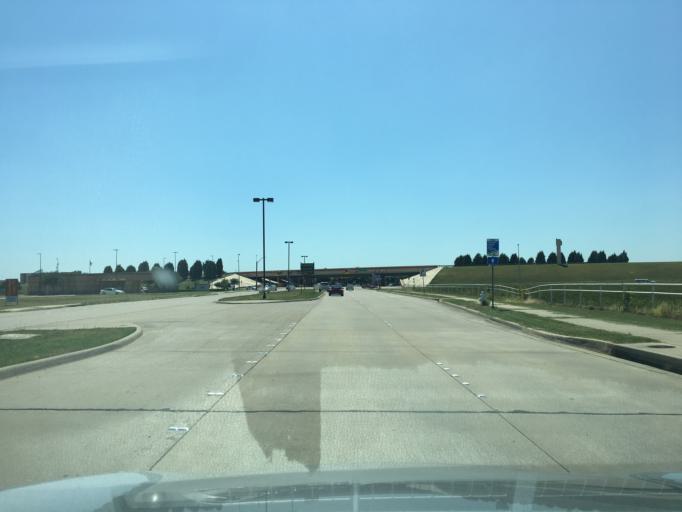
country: US
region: Texas
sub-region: Dallas County
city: Sachse
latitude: 32.9686
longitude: -96.6414
